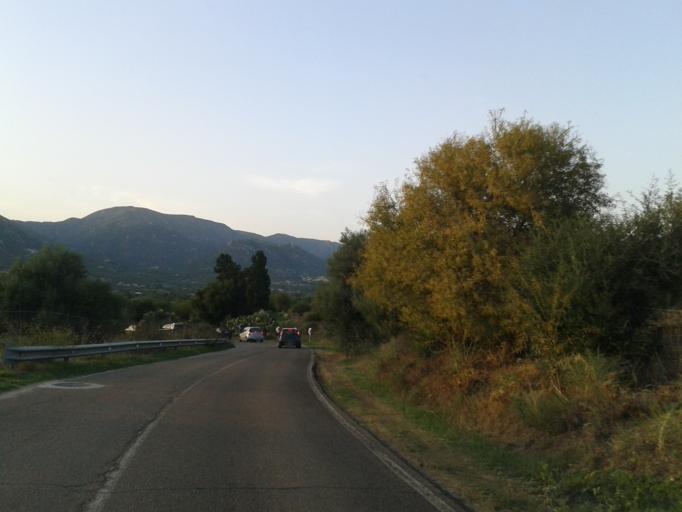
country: IT
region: Sardinia
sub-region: Provincia di Cagliari
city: Villasimius
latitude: 39.1380
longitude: 9.5017
